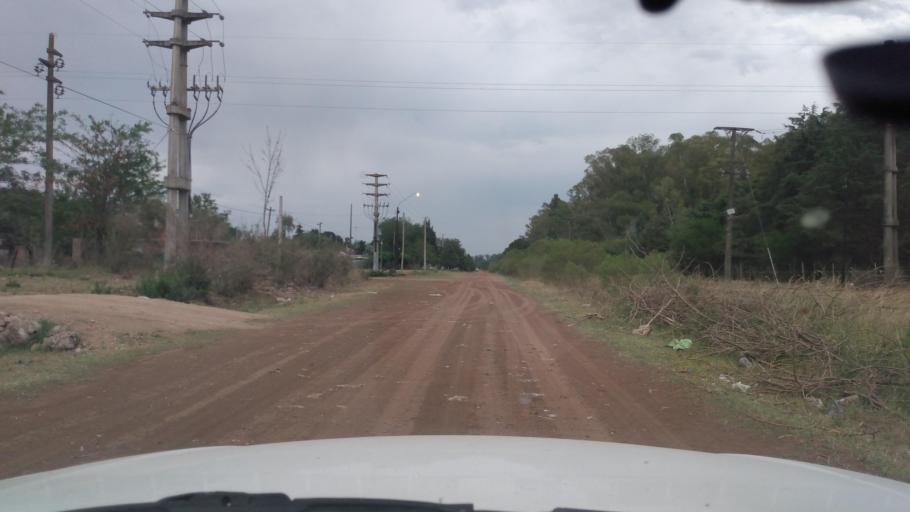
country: AR
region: Buenos Aires
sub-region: Partido de Lujan
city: Lujan
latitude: -34.5589
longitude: -59.1846
